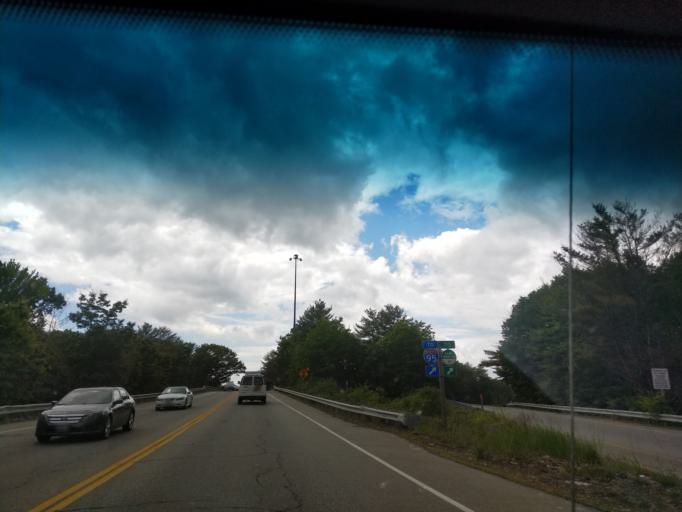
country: US
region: Maine
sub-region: Cumberland County
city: South Portland Gardens
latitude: 43.6261
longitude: -70.3234
